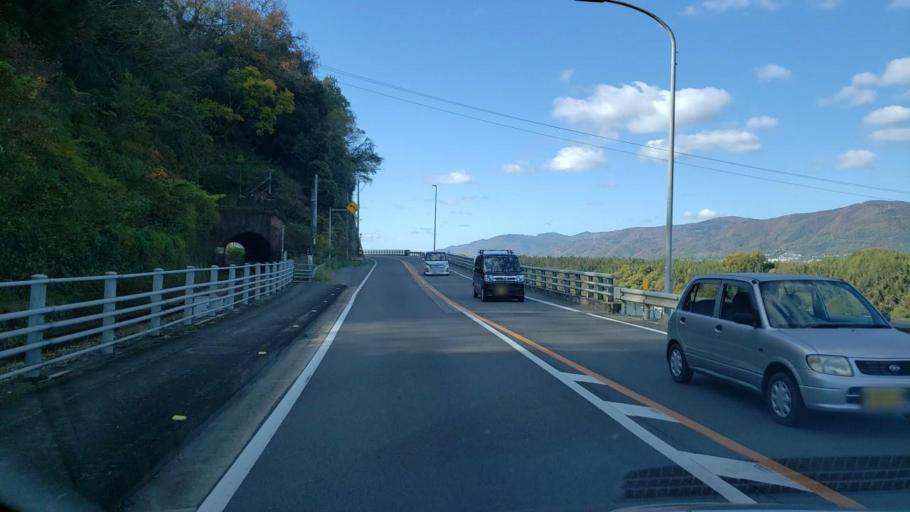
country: JP
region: Tokushima
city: Wakimachi
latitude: 34.0642
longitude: 134.1942
